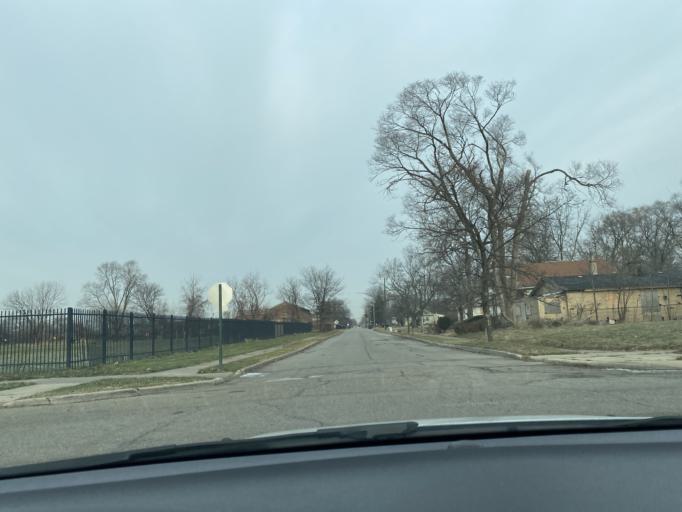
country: US
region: Michigan
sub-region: Wayne County
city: Highland Park
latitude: 42.3732
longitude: -83.1252
